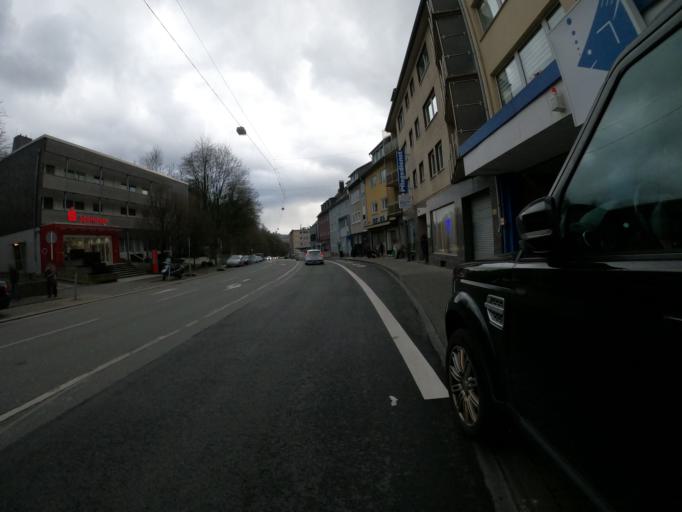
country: DE
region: North Rhine-Westphalia
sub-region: Regierungsbezirk Dusseldorf
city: Wuppertal
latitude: 51.2640
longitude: 7.1564
